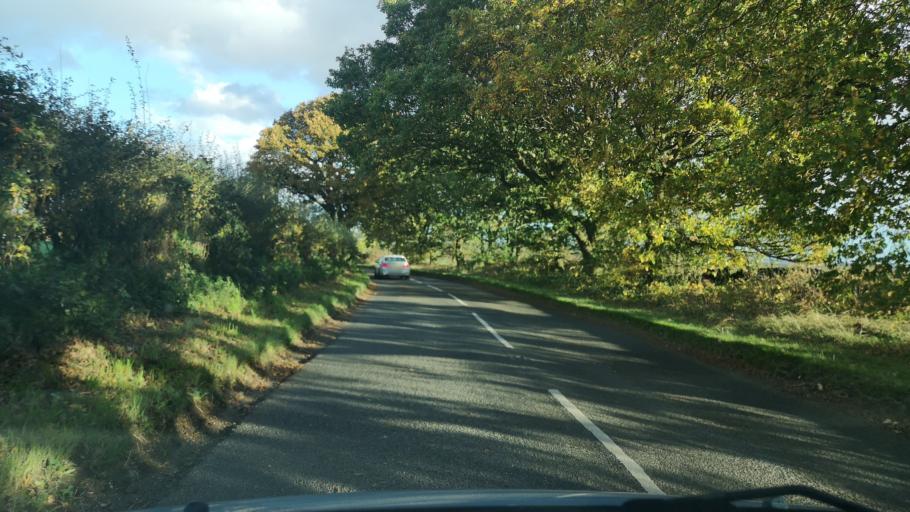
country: GB
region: England
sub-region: City and Borough of Wakefield
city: Woolley
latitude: 53.6204
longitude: -1.5200
